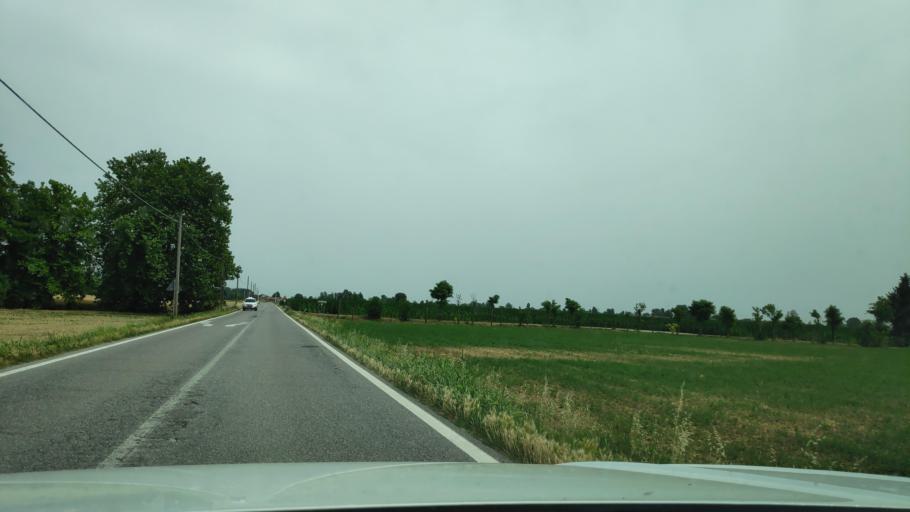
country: IT
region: Lombardy
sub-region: Provincia di Cremona
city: Soncino
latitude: 45.4017
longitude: 9.8452
